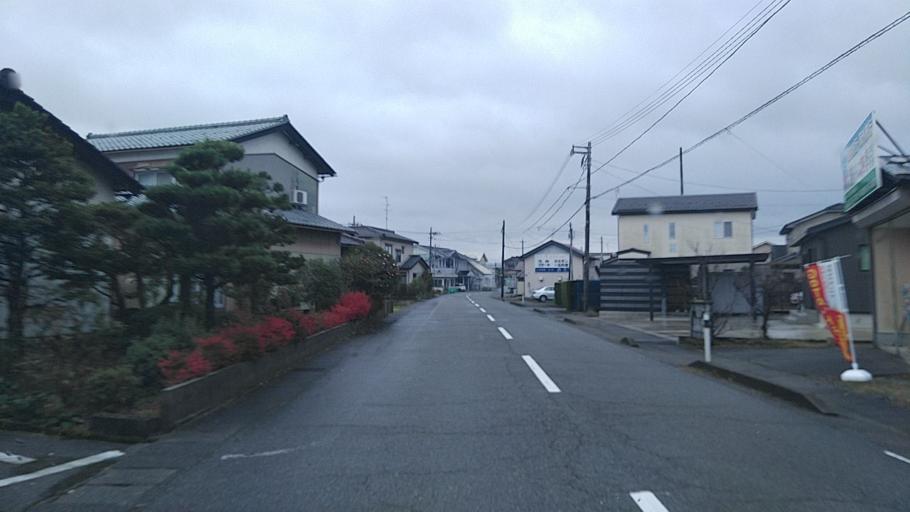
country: JP
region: Ishikawa
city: Komatsu
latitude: 36.3328
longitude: 136.3800
